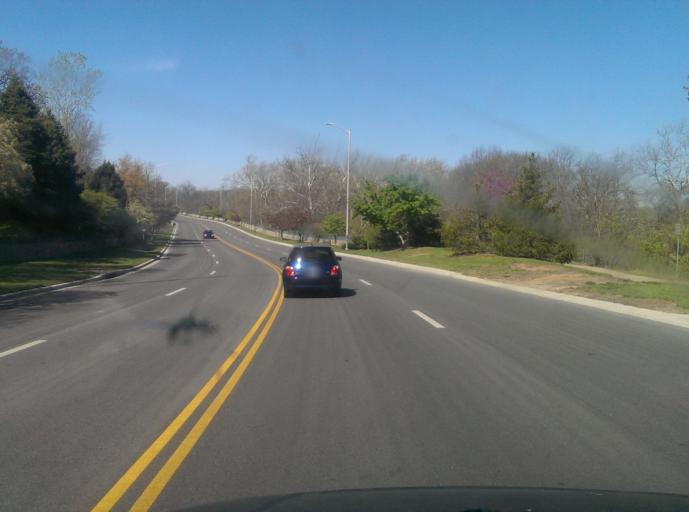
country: US
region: Kansas
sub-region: Johnson County
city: Leawood
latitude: 38.9308
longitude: -94.6125
